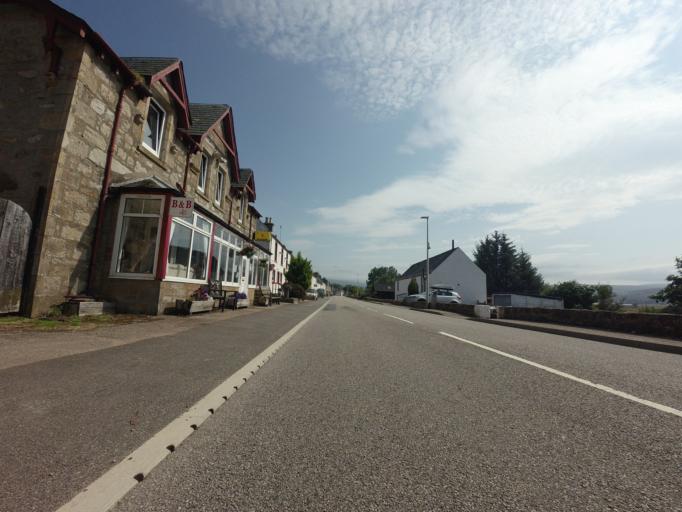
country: GB
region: Scotland
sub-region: Highland
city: Alness
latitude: 57.8950
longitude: -4.3481
